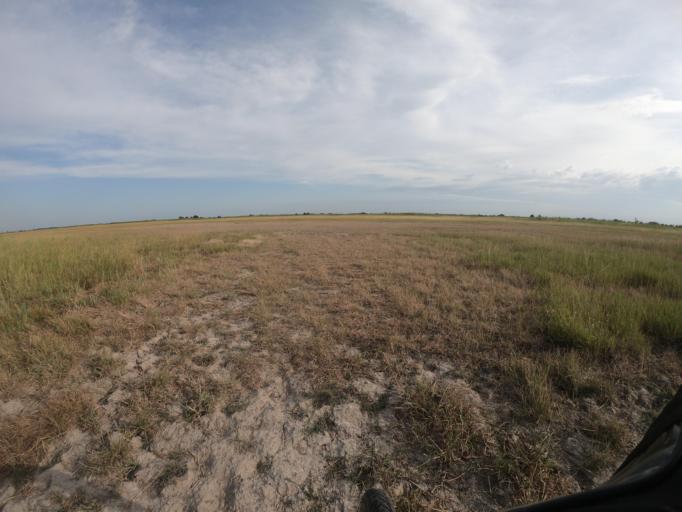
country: HU
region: Hajdu-Bihar
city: Hortobagy
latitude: 47.6020
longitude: 21.0605
